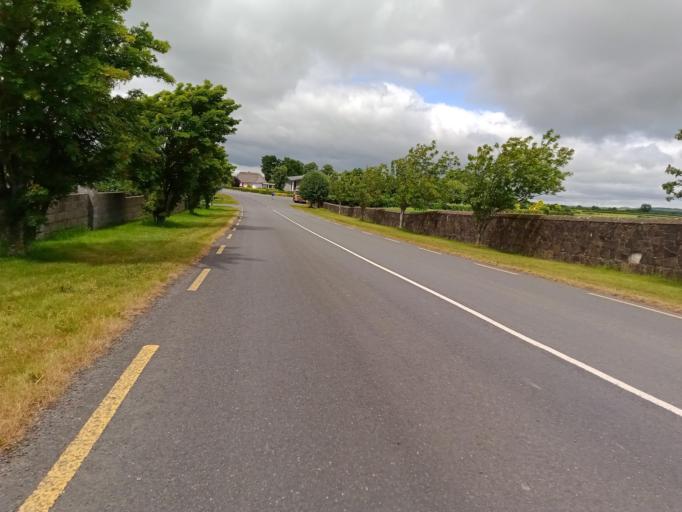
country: IE
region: Leinster
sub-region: Kilkenny
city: Callan
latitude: 52.5510
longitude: -7.3965
